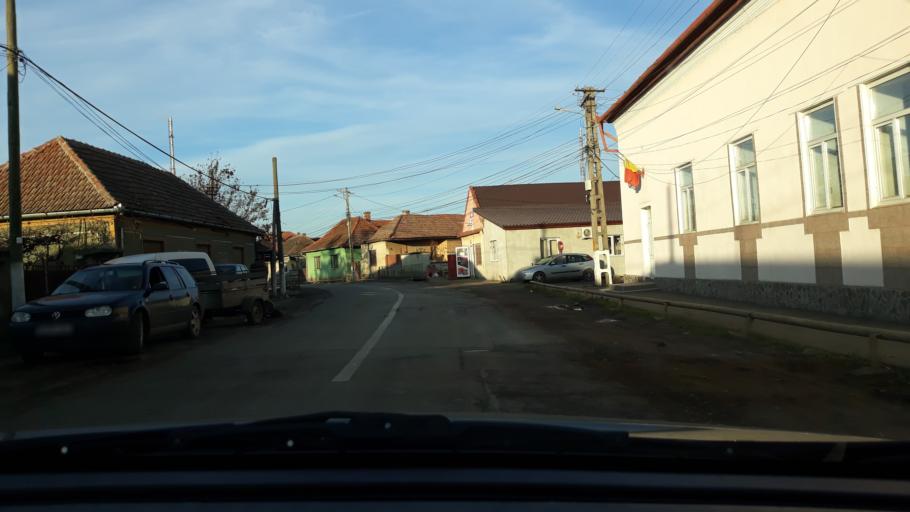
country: RO
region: Bihor
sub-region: Comuna Suplacu de Barcau
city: Suplacu de Barcau
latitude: 47.2556
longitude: 22.5317
